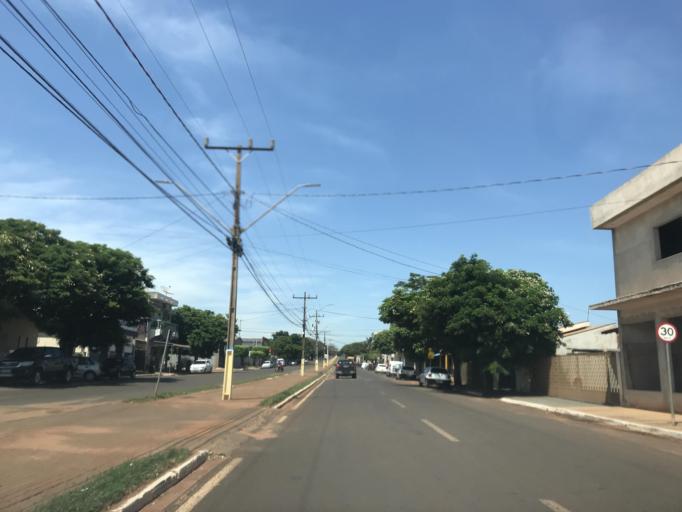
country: BR
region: Parana
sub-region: Paranavai
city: Nova Aurora
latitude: -22.9393
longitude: -52.6895
